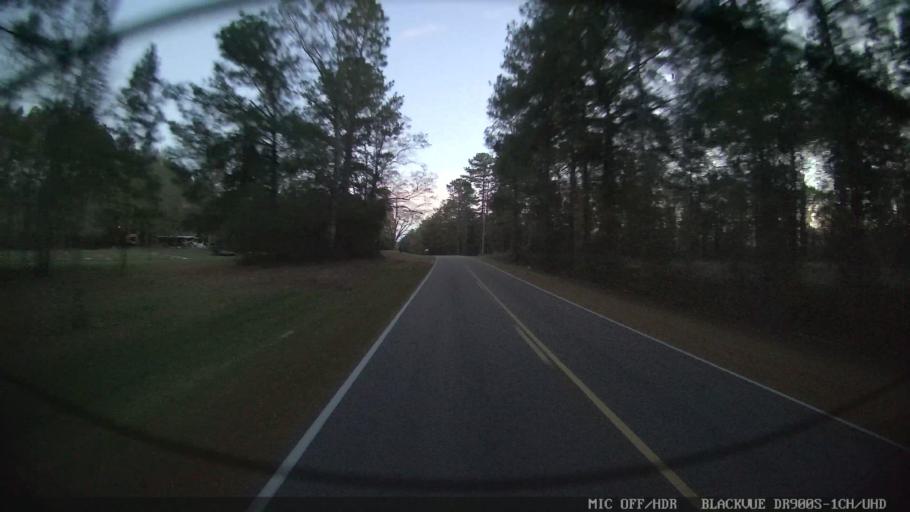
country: US
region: Mississippi
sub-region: Perry County
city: New Augusta
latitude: 31.1082
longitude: -89.1942
